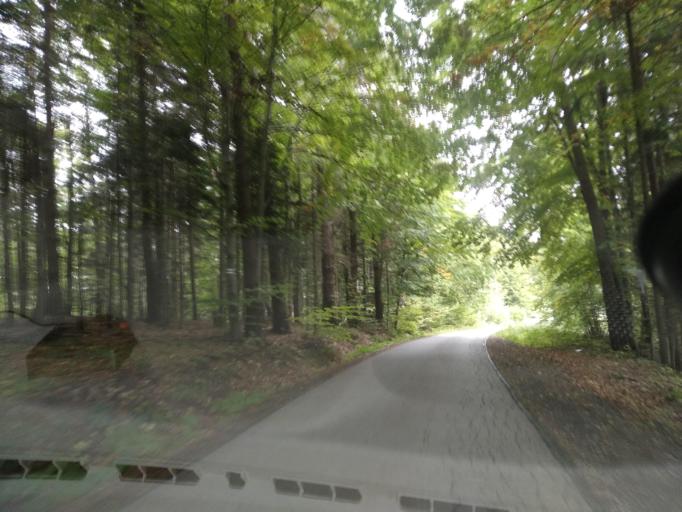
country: PL
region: Lesser Poland Voivodeship
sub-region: Powiat gorlicki
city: Sekowa
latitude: 49.5446
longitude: 21.2405
